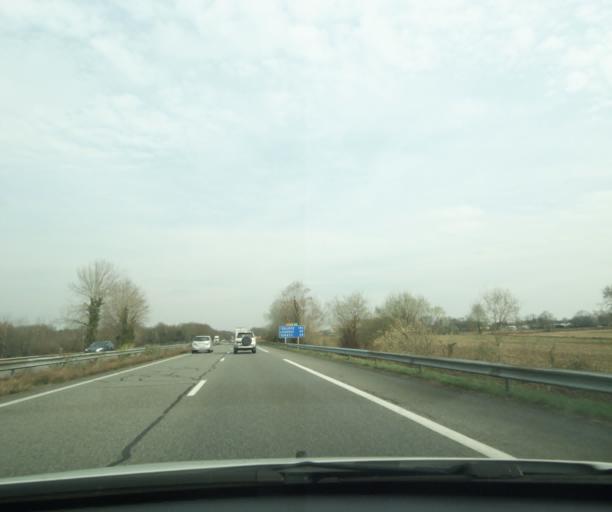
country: FR
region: Aquitaine
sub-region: Departement des Pyrenees-Atlantiques
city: Lescar
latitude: 43.3439
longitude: -0.3966
